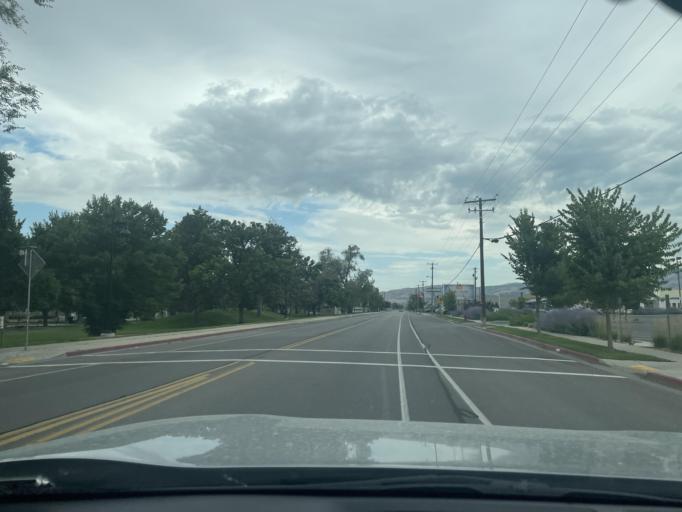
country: US
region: Utah
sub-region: Salt Lake County
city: Centerfield
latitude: 40.6887
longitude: -111.8910
